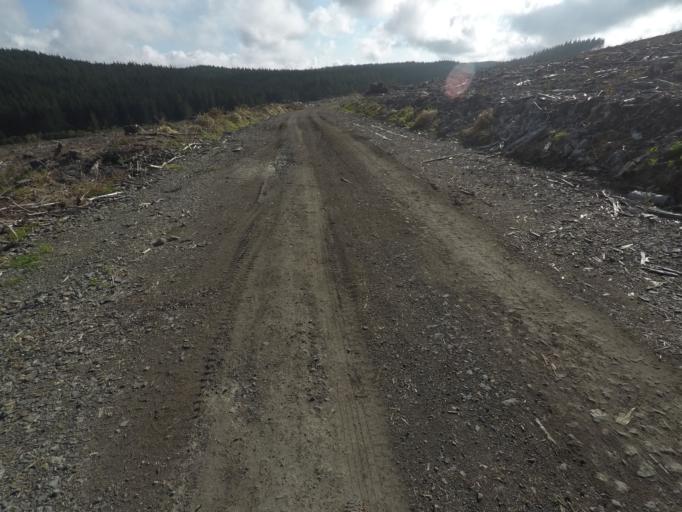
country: NZ
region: Auckland
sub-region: Auckland
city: Parakai
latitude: -36.7138
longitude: 174.5678
